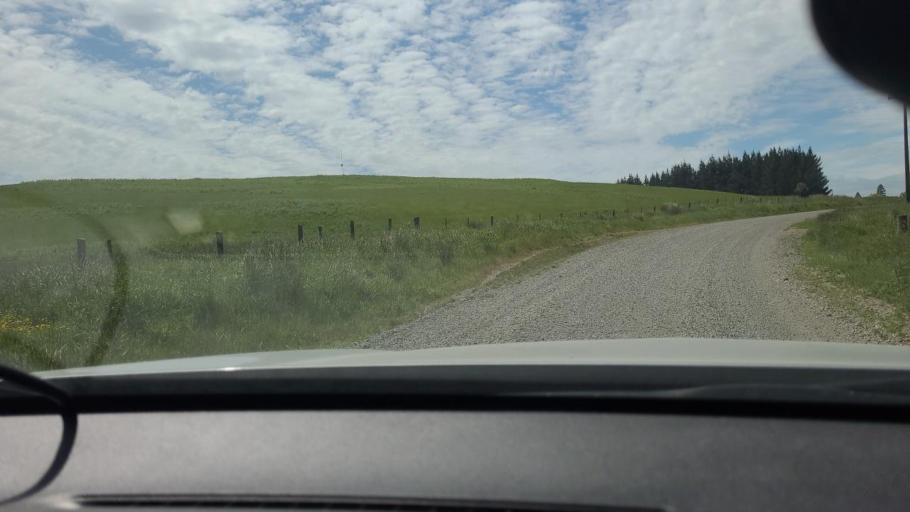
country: NZ
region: Southland
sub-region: Southland District
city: Riverton
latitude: -45.9444
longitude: 167.8983
